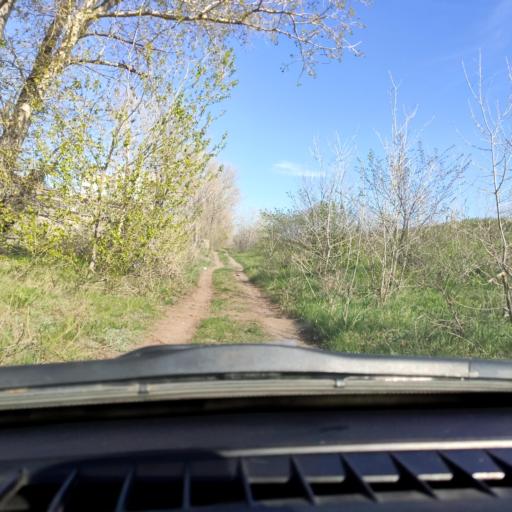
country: RU
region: Samara
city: Zhigulevsk
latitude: 53.4614
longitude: 49.5447
